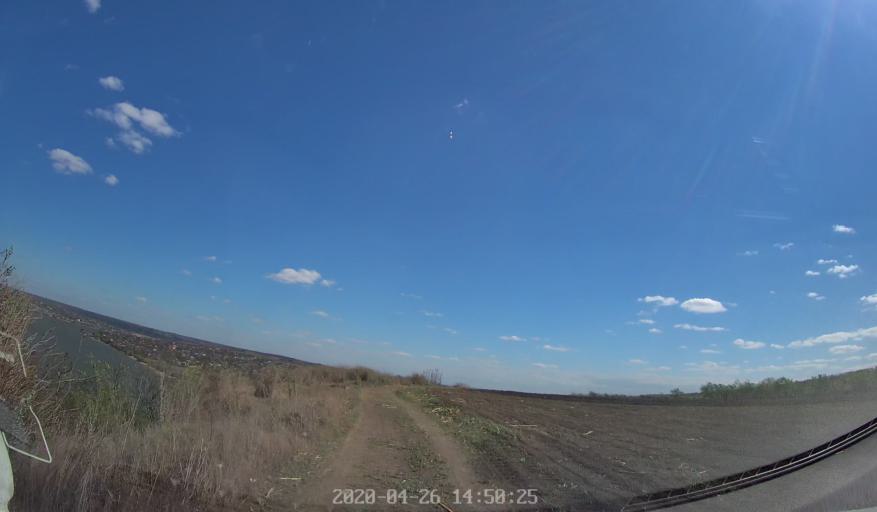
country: MD
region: Telenesti
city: Cocieri
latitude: 47.3581
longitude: 29.0652
